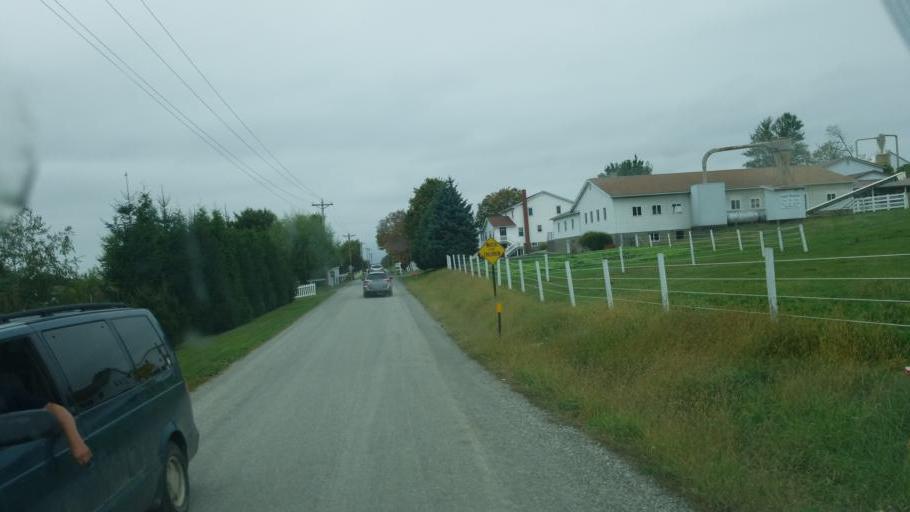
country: US
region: Ohio
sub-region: Wayne County
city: Apple Creek
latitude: 40.6532
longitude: -81.7844
